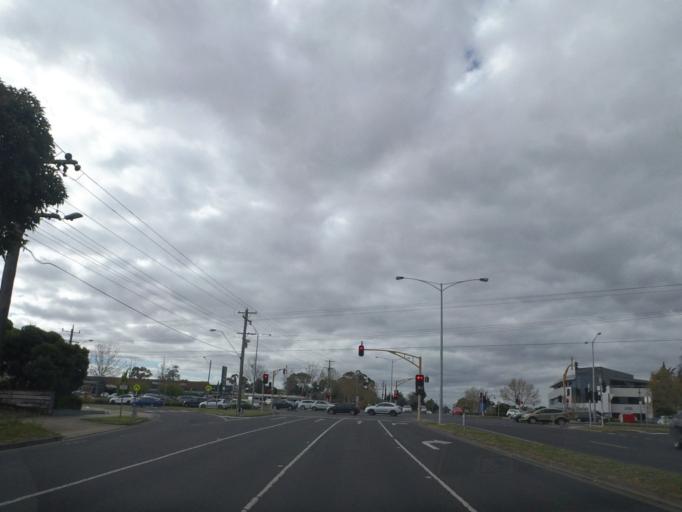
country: AU
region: Victoria
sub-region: Manningham
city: Templestowe Lower
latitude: -37.7743
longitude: 145.1140
